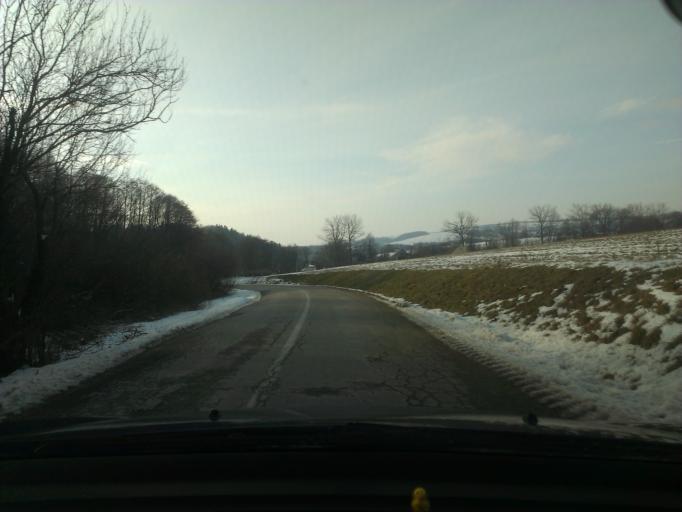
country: SK
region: Trenciansky
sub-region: Okres Myjava
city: Myjava
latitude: 48.7760
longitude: 17.5841
